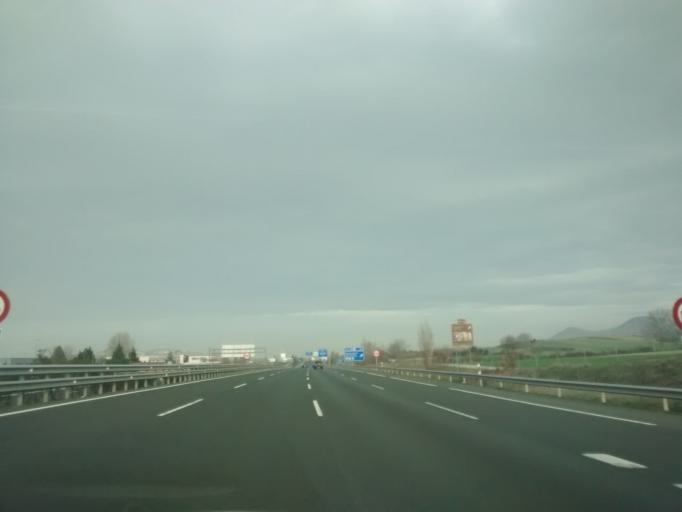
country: ES
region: Basque Country
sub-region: Provincia de Alava
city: Arminon
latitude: 42.8132
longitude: -2.7924
